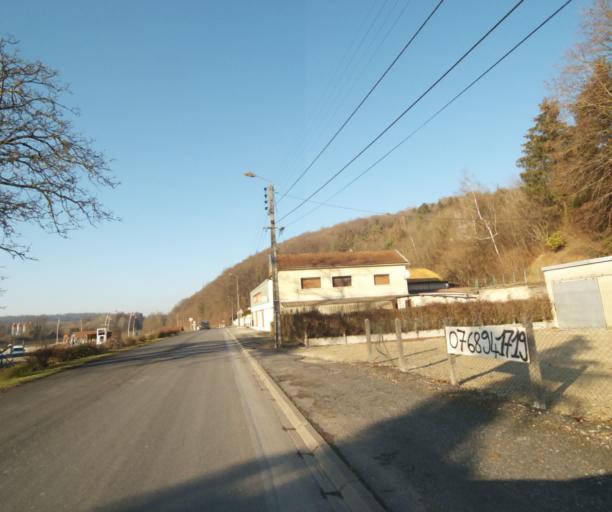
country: FR
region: Champagne-Ardenne
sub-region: Departement de la Haute-Marne
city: Chevillon
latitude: 48.5253
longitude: 5.1124
